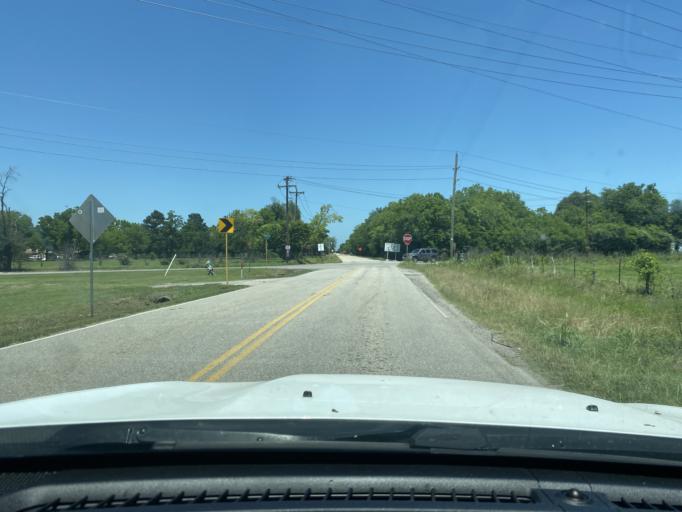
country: US
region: Texas
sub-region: Waller County
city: Waller
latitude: 30.0214
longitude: -95.8485
